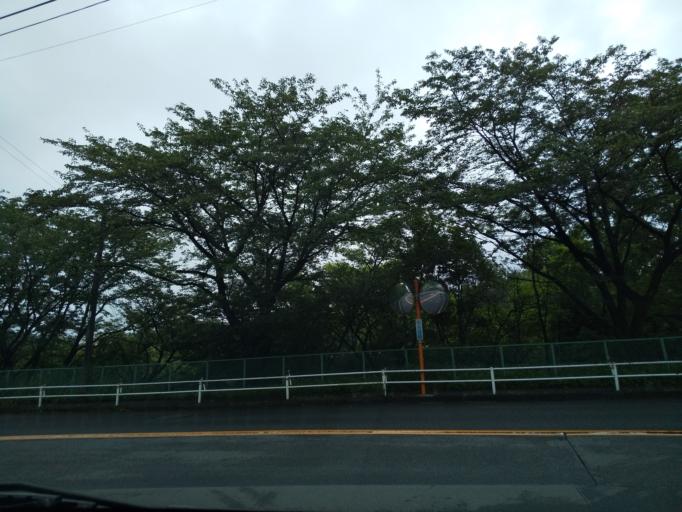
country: JP
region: Tokyo
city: Hino
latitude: 35.6530
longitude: 139.4163
